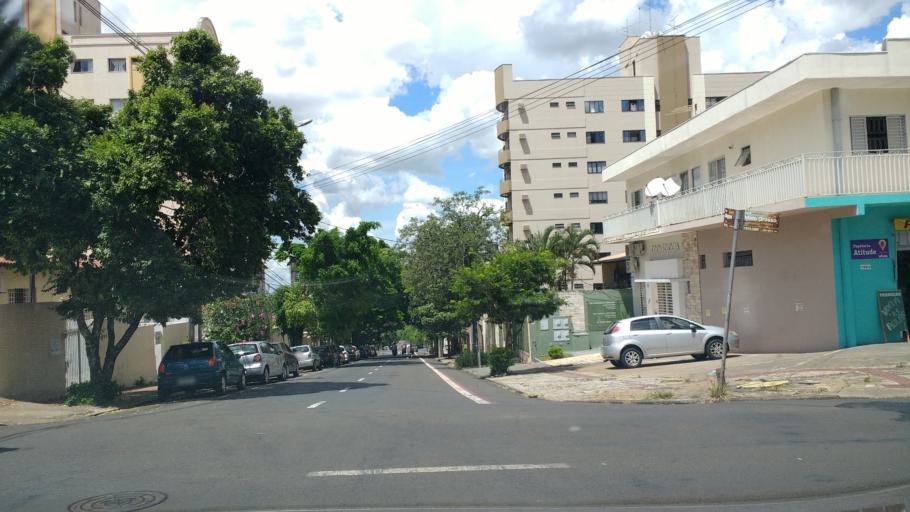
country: BR
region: Parana
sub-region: Londrina
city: Londrina
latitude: -23.3176
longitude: -51.1564
